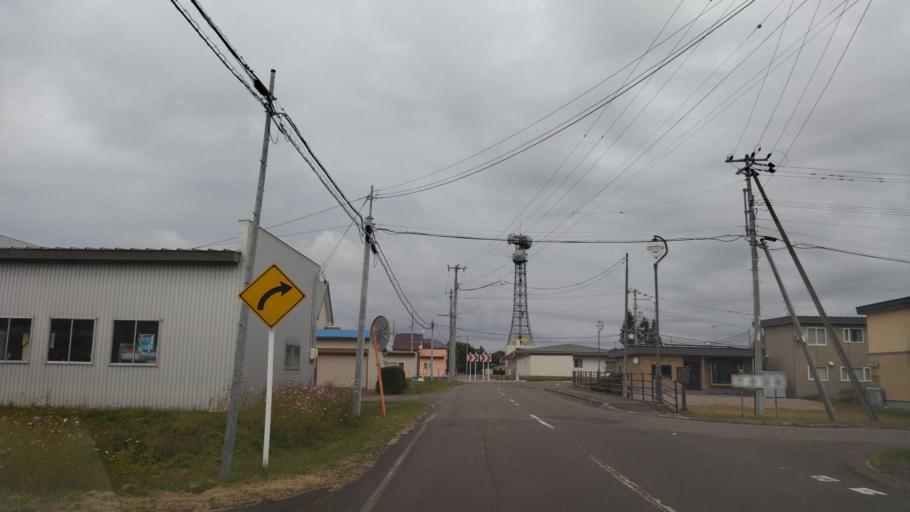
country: JP
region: Hokkaido
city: Otofuke
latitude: 43.2239
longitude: 143.2861
